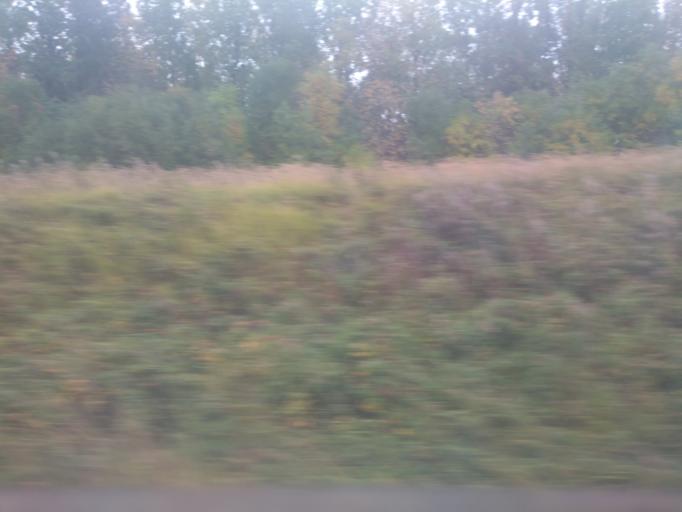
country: RU
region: Udmurtiya
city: Alnashi
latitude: 56.2586
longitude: 52.7601
